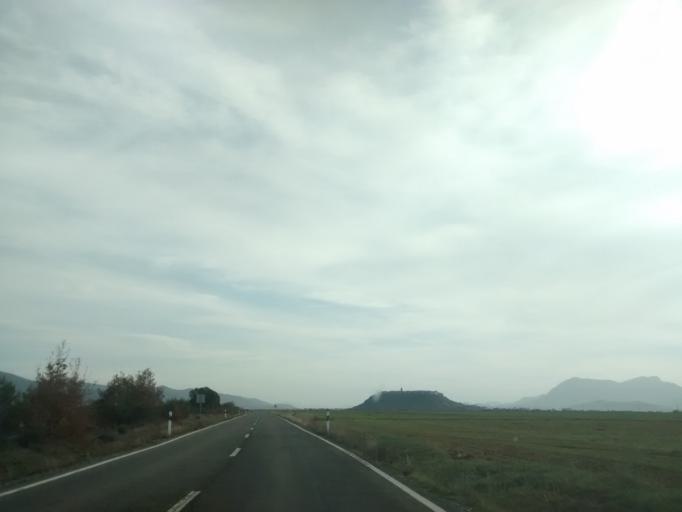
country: ES
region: Aragon
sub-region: Provincia de Zaragoza
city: Mianos
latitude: 42.6109
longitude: -0.8877
